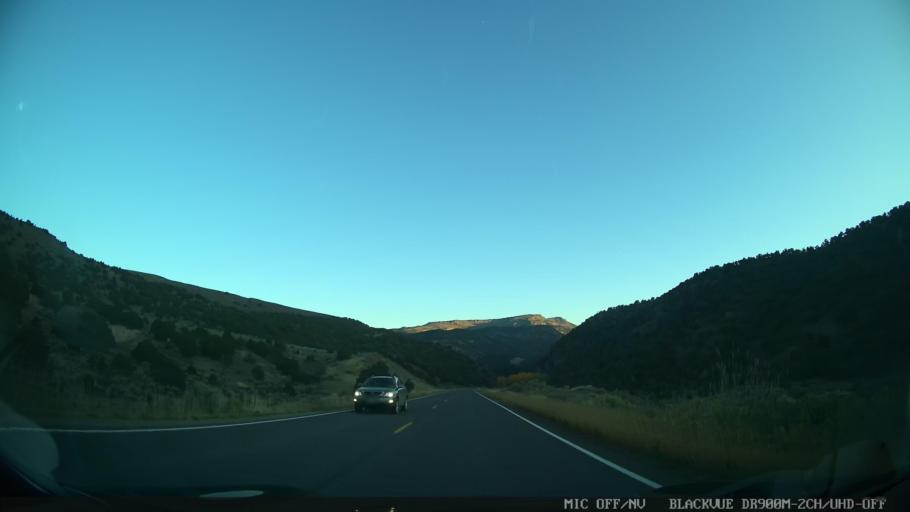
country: US
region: Colorado
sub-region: Eagle County
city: Edwards
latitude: 39.8429
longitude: -106.6424
